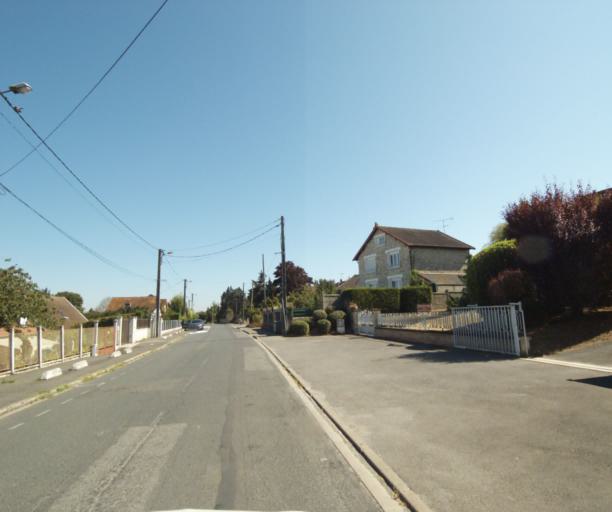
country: FR
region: Ile-de-France
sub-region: Departement de l'Essonne
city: Itteville
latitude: 48.5191
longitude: 2.3479
